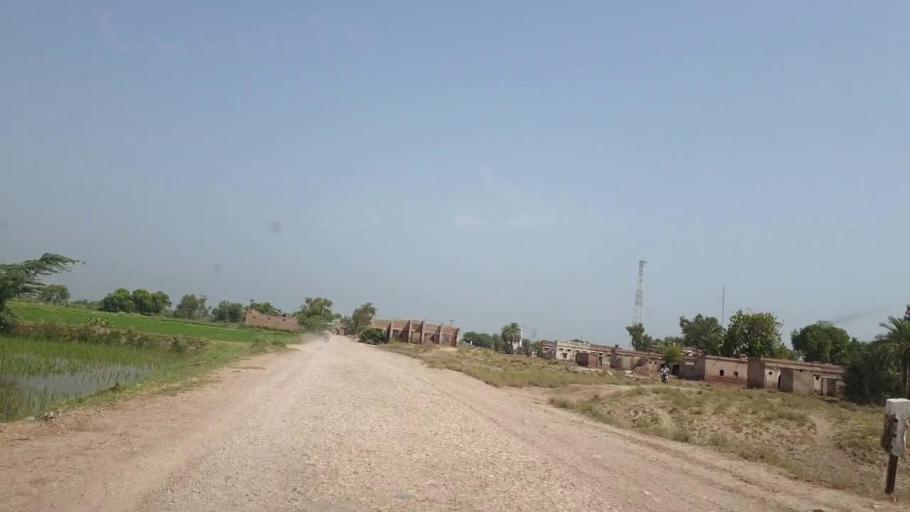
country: PK
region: Sindh
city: Lakhi
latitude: 27.8696
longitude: 68.6608
